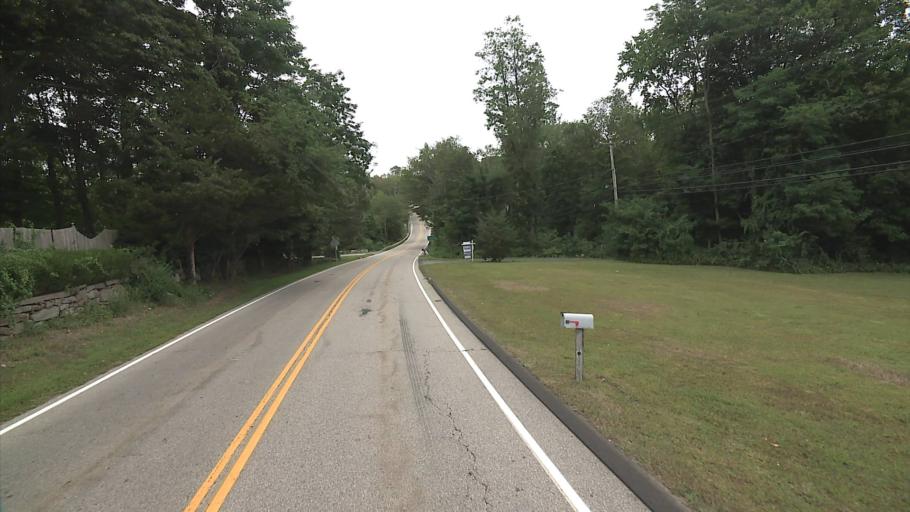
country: US
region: Connecticut
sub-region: Middlesex County
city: Essex Village
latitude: 41.3815
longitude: -72.3500
